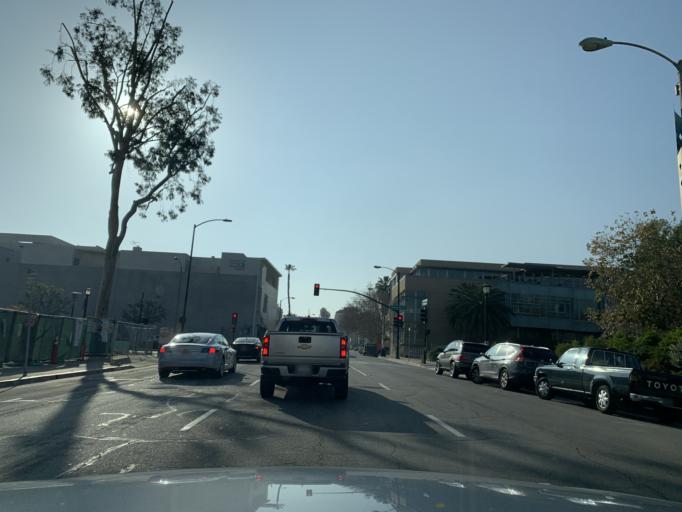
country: US
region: California
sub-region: Los Angeles County
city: Pasadena
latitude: 34.1472
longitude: -118.1393
